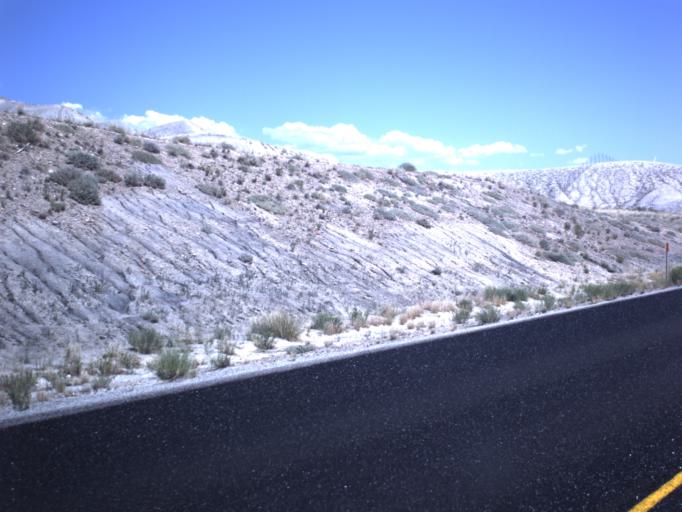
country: US
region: Utah
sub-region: Emery County
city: Ferron
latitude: 39.0274
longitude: -111.1323
